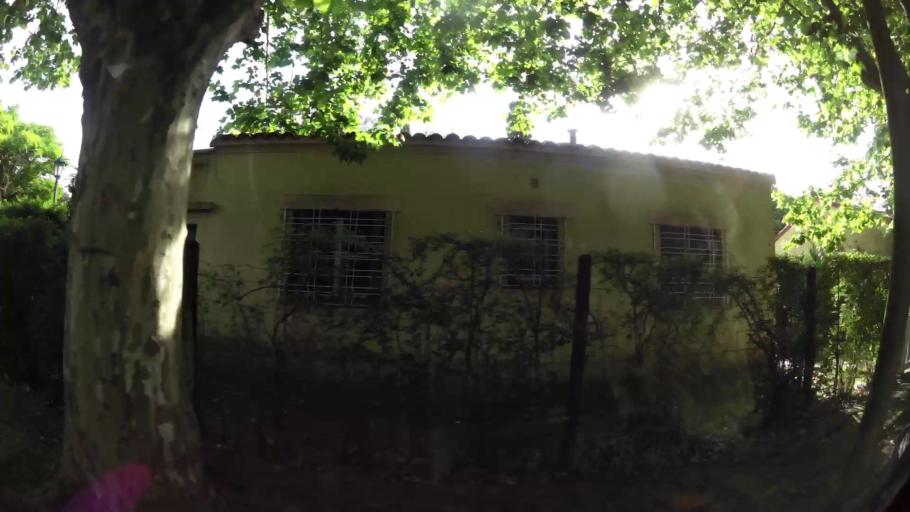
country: AR
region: Buenos Aires
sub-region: Partido de Quilmes
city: Quilmes
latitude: -34.7357
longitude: -58.2566
